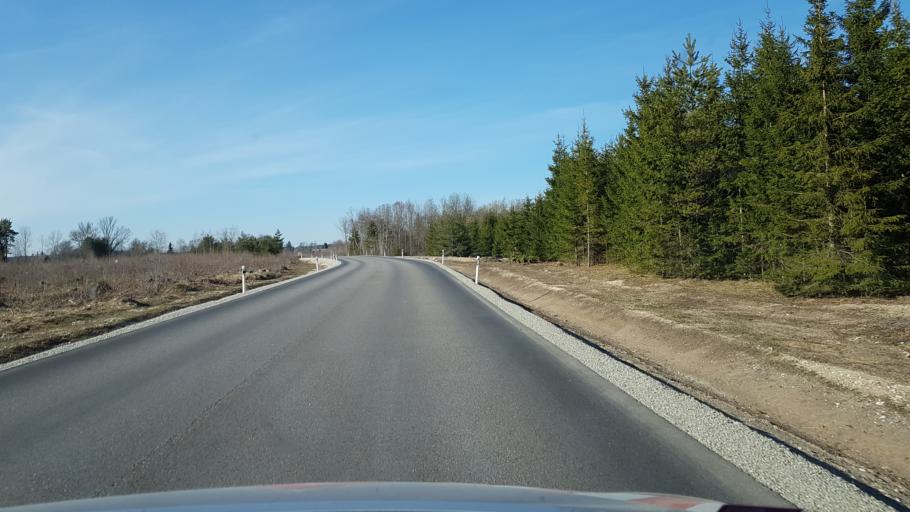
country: EE
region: Laeaene-Virumaa
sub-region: Vinni vald
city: Vinni
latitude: 59.1392
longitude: 26.5976
